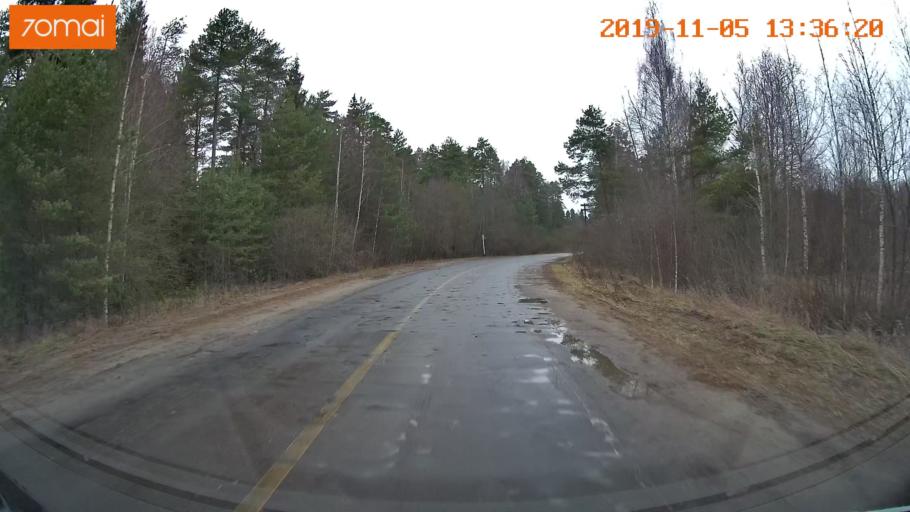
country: RU
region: Ivanovo
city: Shuya
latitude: 56.9139
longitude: 41.3827
